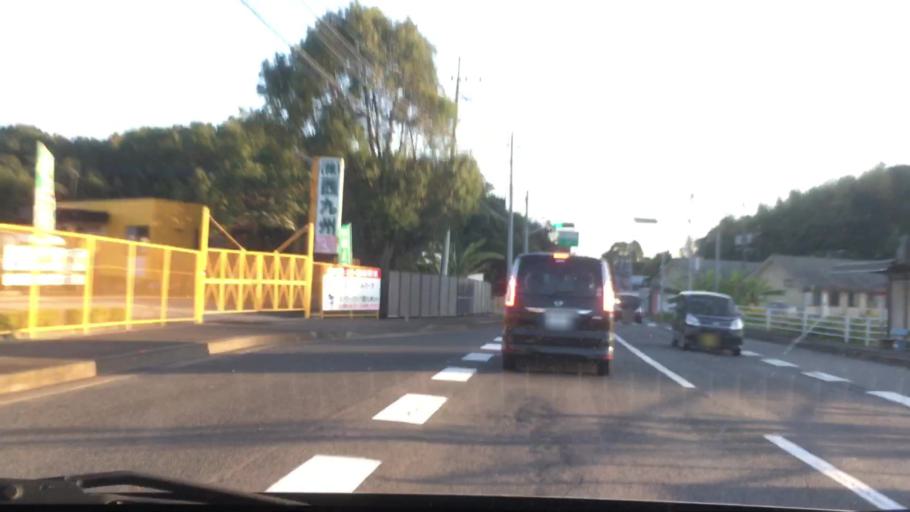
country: JP
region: Nagasaki
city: Sasebo
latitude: 33.0660
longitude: 129.7643
